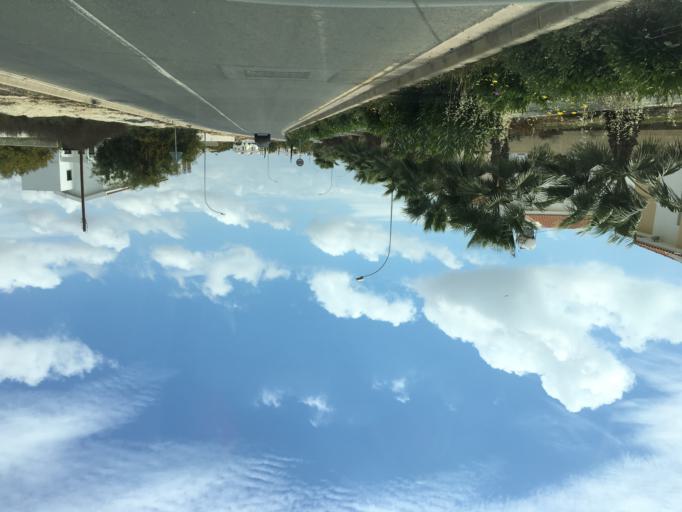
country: CY
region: Ammochostos
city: Liopetri
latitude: 34.9812
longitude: 33.9314
